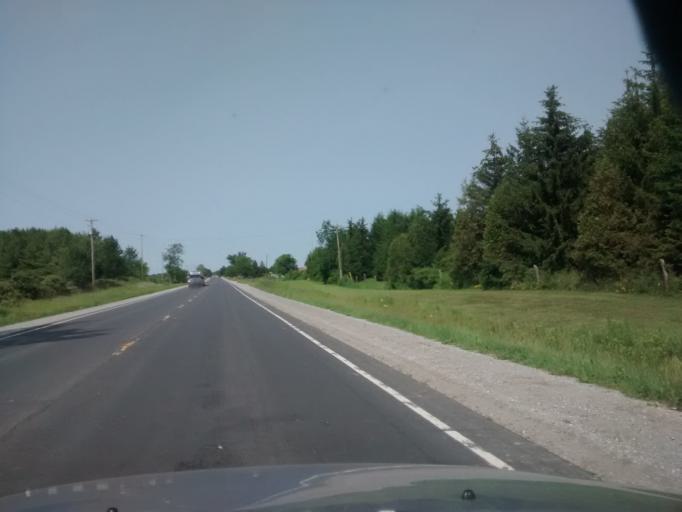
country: CA
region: Ontario
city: Hamilton
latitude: 42.9632
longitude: -79.8024
